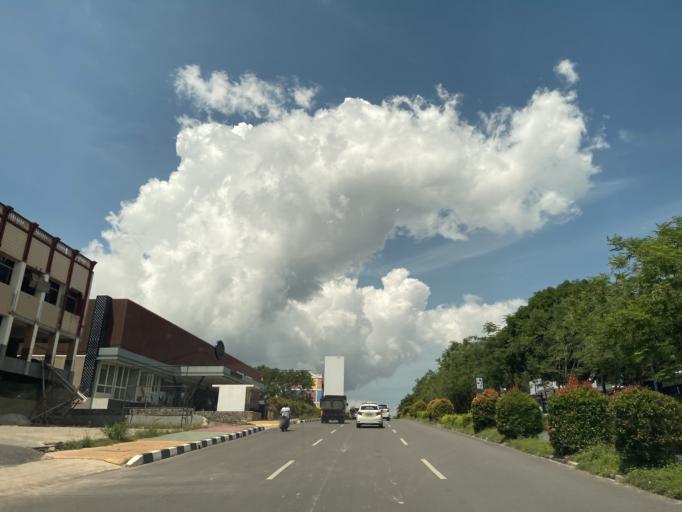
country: SG
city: Singapore
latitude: 1.1363
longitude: 104.0168
